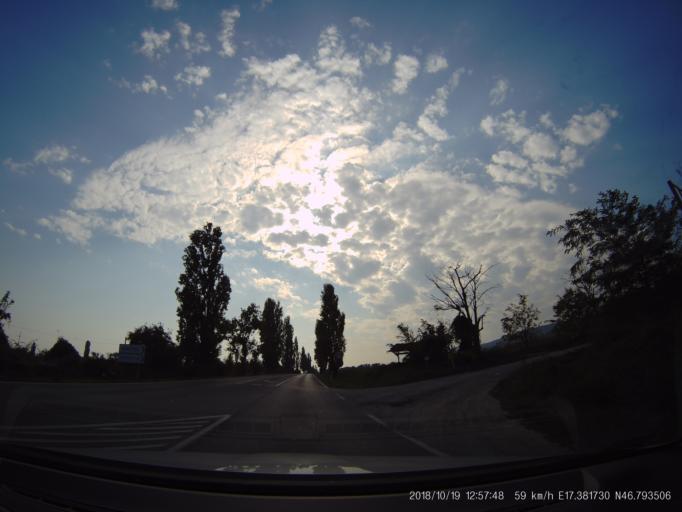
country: HU
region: Zala
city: Vonyarcvashegy
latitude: 46.7935
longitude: 17.3817
